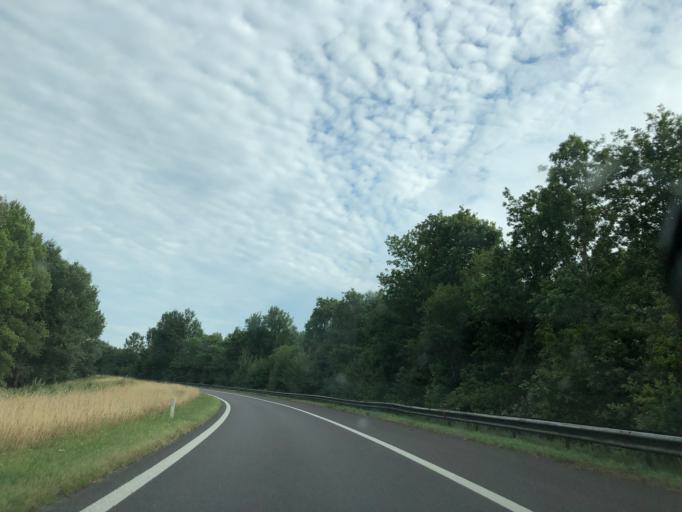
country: NL
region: Drenthe
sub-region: Gemeente Tynaarlo
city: Tynaarlo
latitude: 53.1124
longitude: 6.6091
